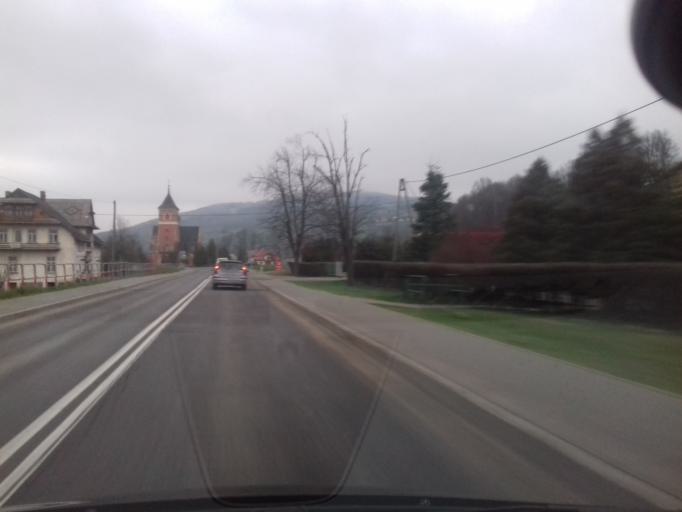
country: PL
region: Lesser Poland Voivodeship
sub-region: Powiat limanowski
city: Mszana Dolna
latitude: 49.7015
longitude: 20.0387
